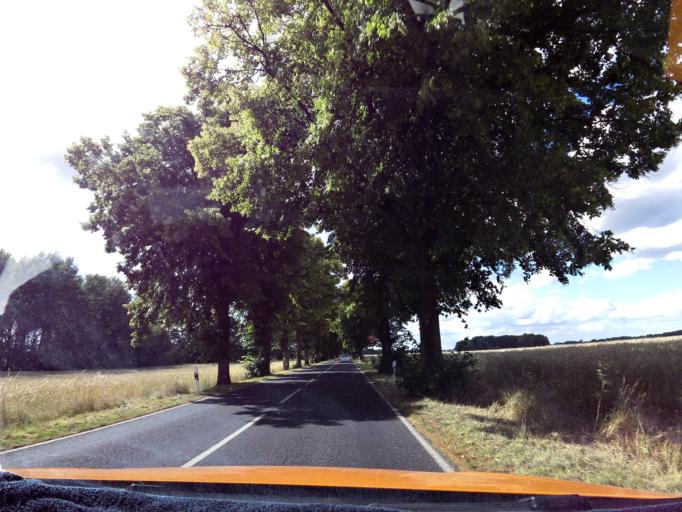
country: DE
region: Brandenburg
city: Mittenwalde
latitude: 52.2988
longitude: 13.5275
